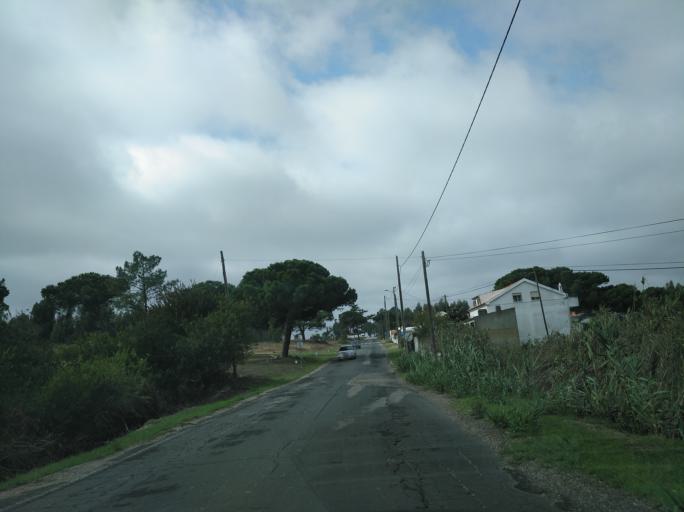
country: PT
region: Setubal
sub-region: Santiago do Cacem
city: Santo Andre
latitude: 38.1316
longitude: -8.7762
